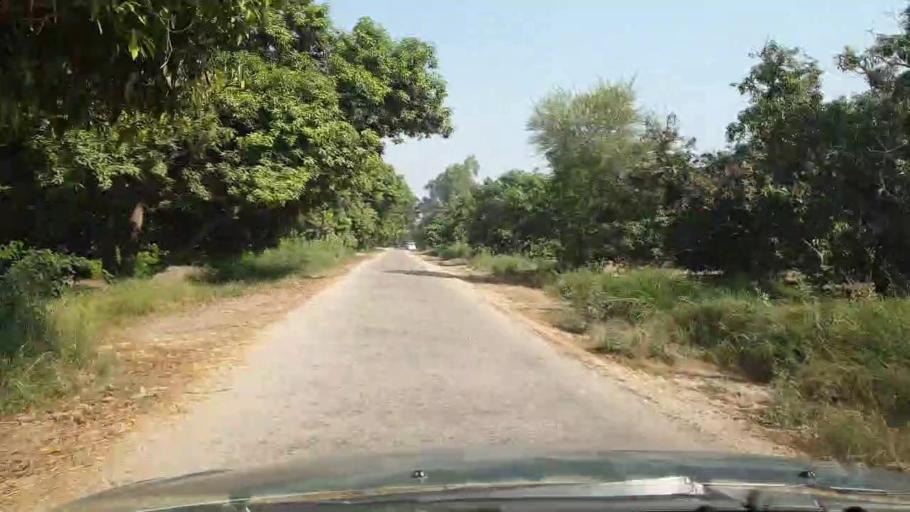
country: PK
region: Sindh
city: Tando Jam
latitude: 25.3282
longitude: 68.5409
